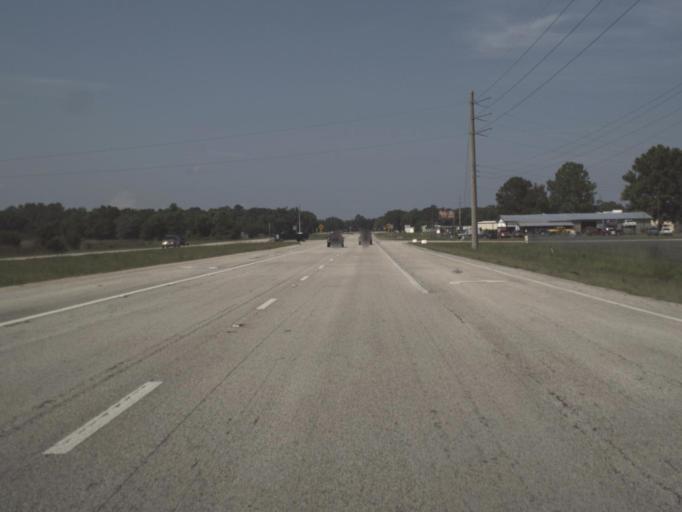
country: US
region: Florida
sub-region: Putnam County
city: East Palatka
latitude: 29.7220
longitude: -81.4869
